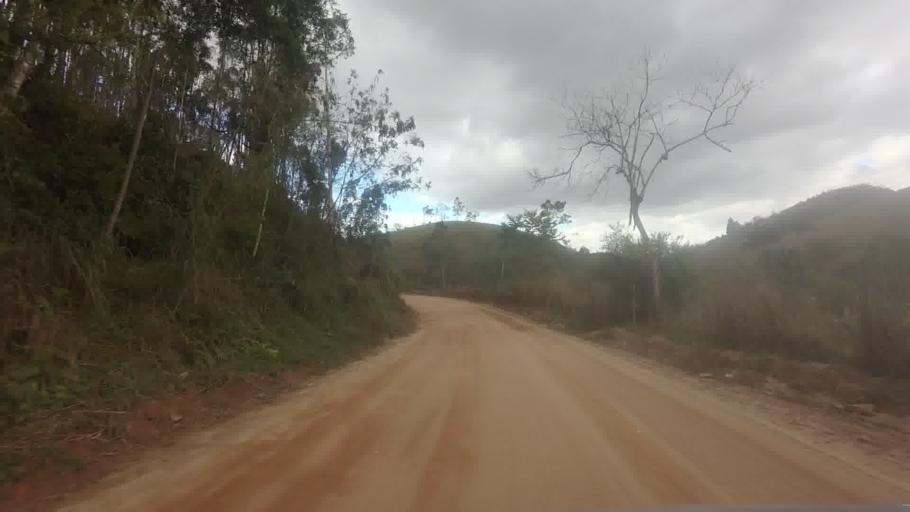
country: BR
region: Espirito Santo
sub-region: Mimoso Do Sul
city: Mimoso do Sul
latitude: -20.9470
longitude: -41.4080
